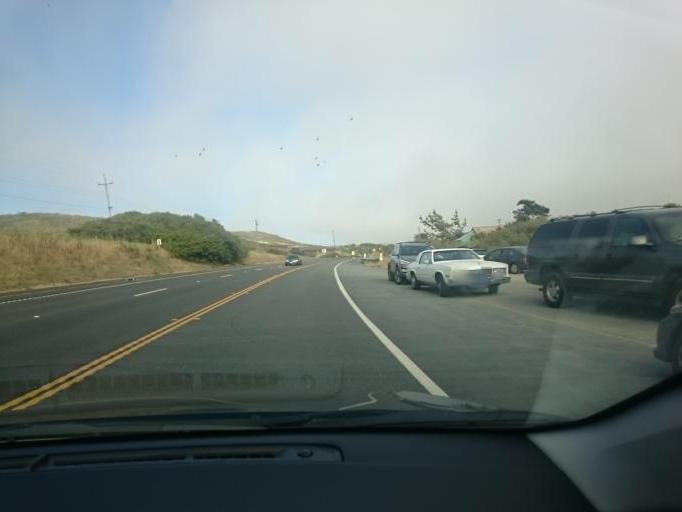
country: US
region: California
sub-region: Santa Cruz County
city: Bonny Doon
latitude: 36.9702
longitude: -122.1193
